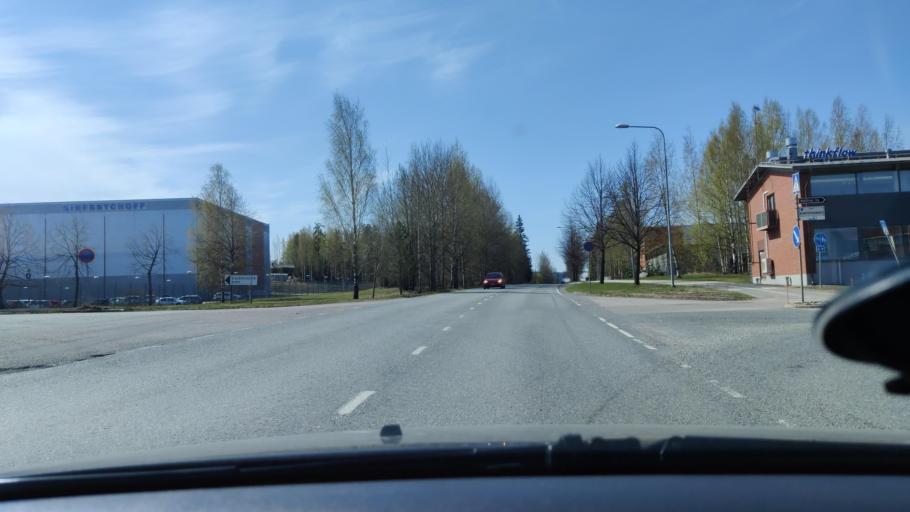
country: FI
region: Uusimaa
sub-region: Helsinki
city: Kerava
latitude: 60.3820
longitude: 25.1086
